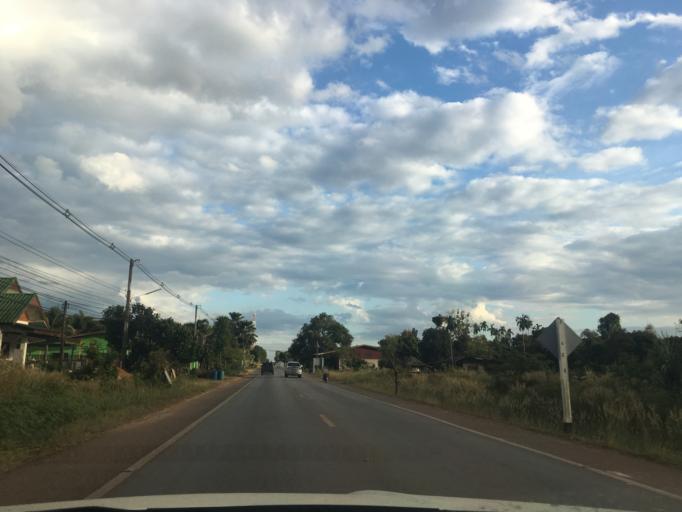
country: TH
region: Chanthaburi
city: Na Yai Am
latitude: 12.7406
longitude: 101.7382
